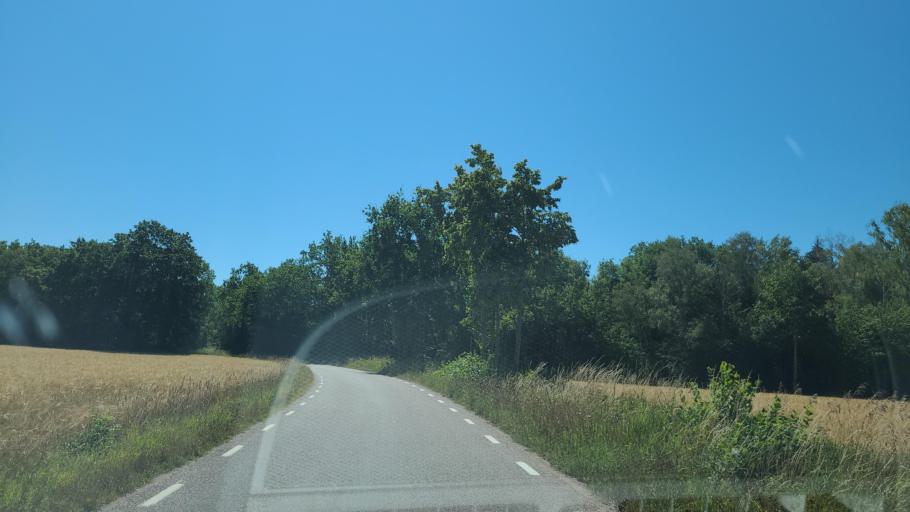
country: SE
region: Kalmar
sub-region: Borgholms Kommun
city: Borgholm
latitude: 56.7486
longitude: 16.6588
